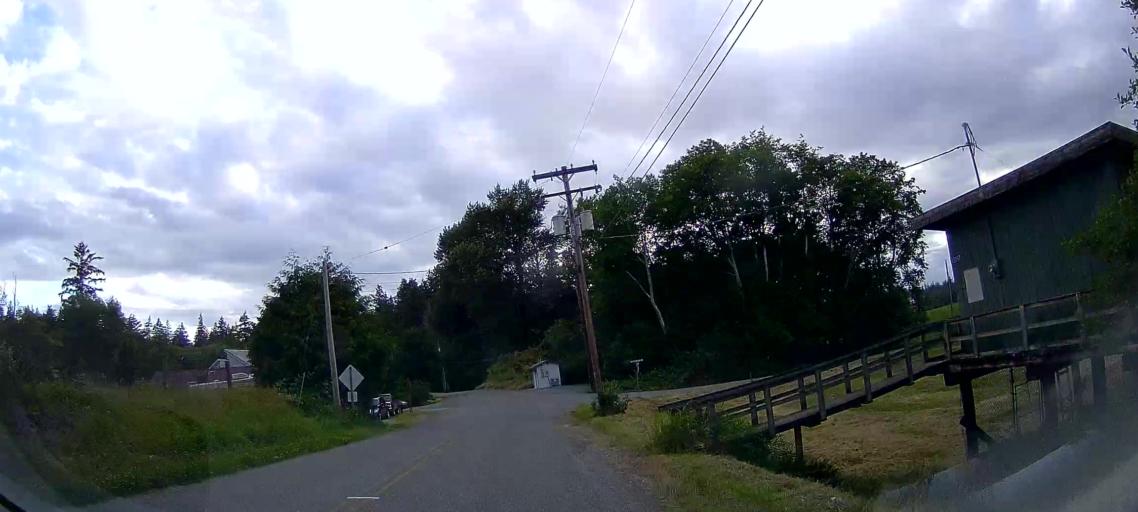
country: US
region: Washington
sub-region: Skagit County
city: Mount Vernon
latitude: 48.3660
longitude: -122.4202
